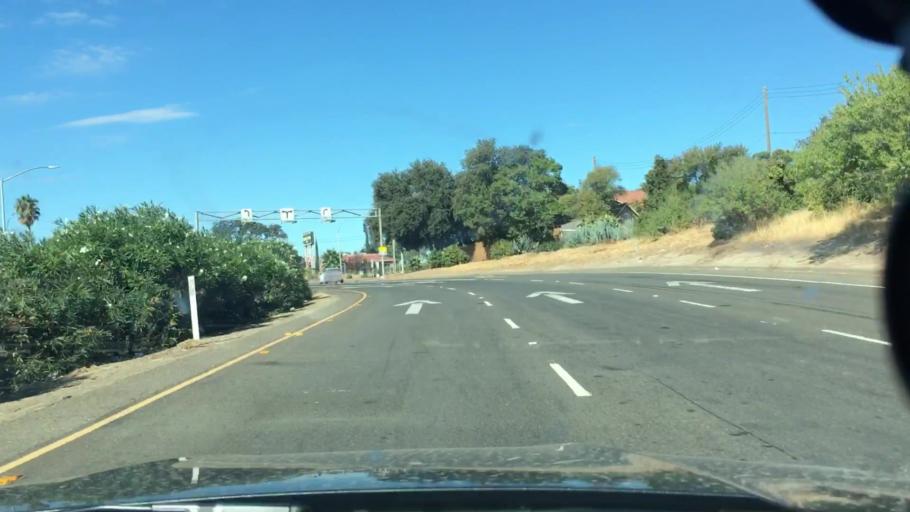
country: US
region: California
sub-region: Sacramento County
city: North Highlands
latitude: 38.6467
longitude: -121.3817
